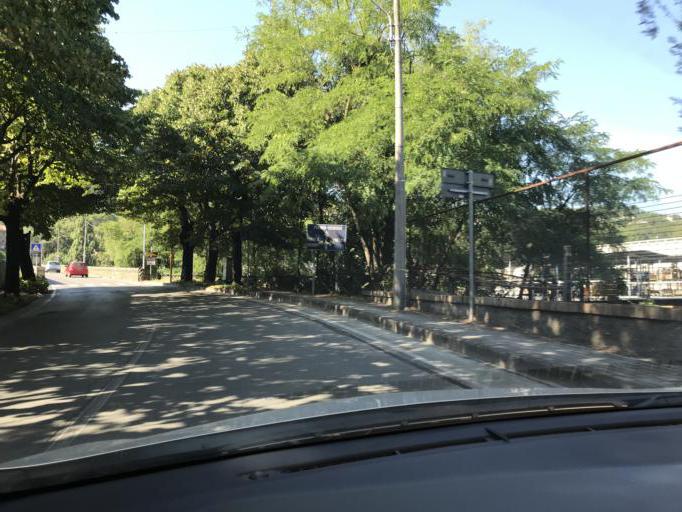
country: IT
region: Umbria
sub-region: Provincia di Perugia
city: Ponte Felcino
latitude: 43.1097
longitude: 12.4463
